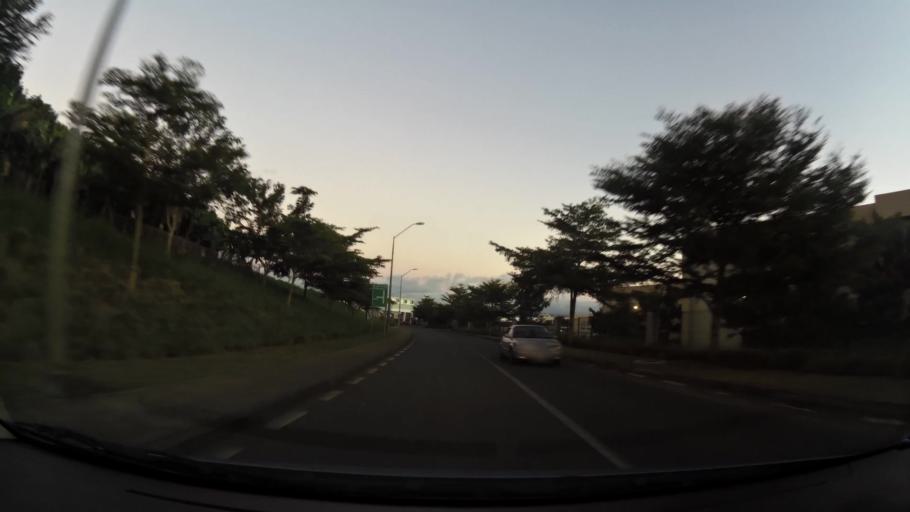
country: MU
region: Moka
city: Moka
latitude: -20.2243
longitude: 57.4981
